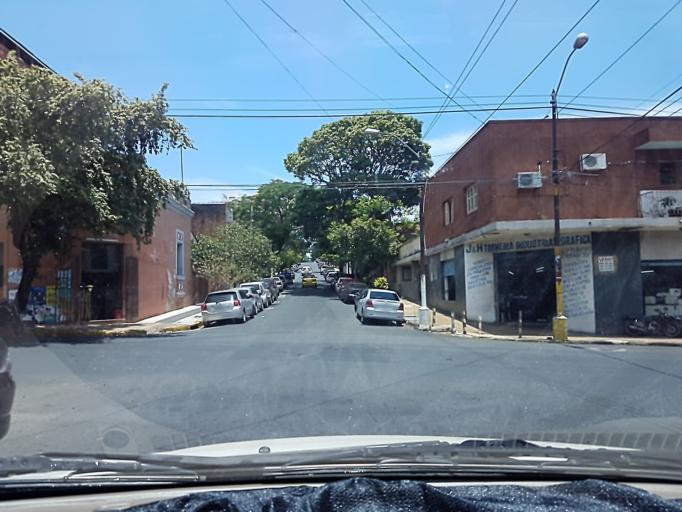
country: PY
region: Asuncion
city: Asuncion
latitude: -25.2898
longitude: -57.6354
